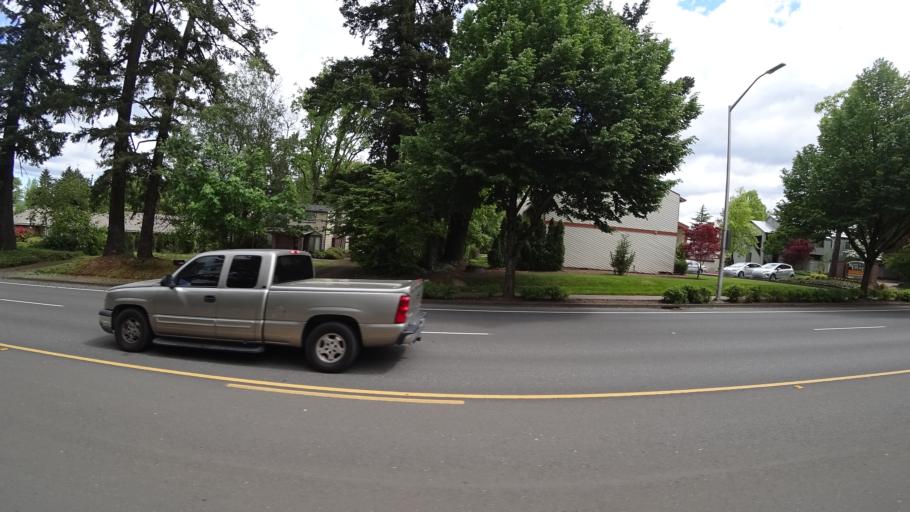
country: US
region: Oregon
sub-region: Washington County
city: Beaverton
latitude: 45.4708
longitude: -122.8046
